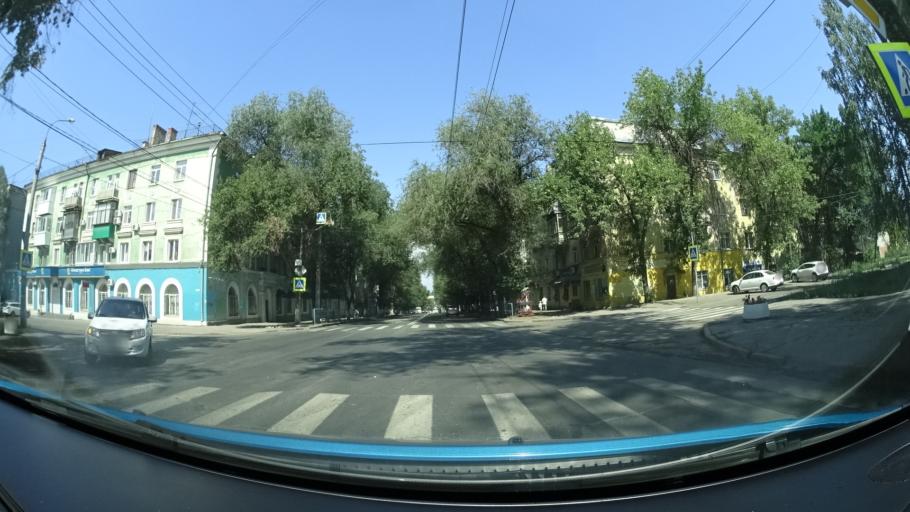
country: RU
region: Samara
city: Samara
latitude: 53.2085
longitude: 50.1589
